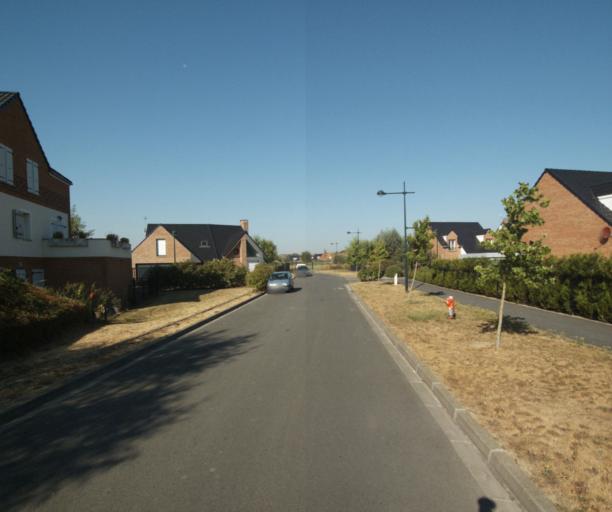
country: FR
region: Nord-Pas-de-Calais
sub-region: Departement du Nord
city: Wervicq-Sud
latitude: 50.7762
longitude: 3.0517
